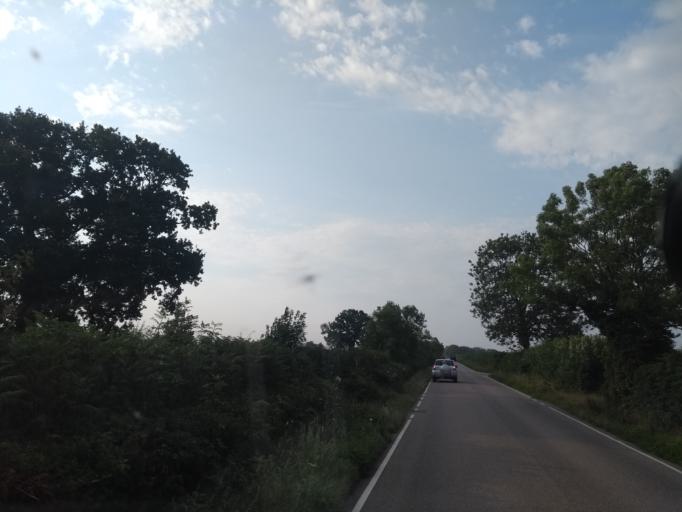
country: GB
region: England
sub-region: Devon
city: Honiton
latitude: 50.8370
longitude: -3.1093
